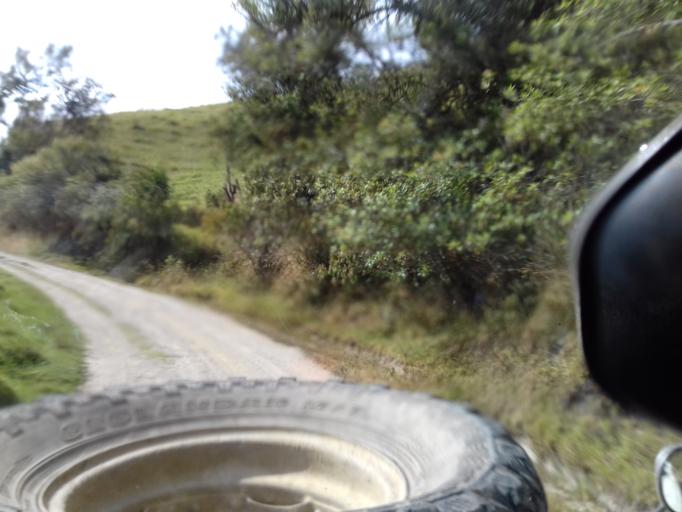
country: CO
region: Tolima
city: Cajamarca
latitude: 4.5431
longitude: -75.4845
